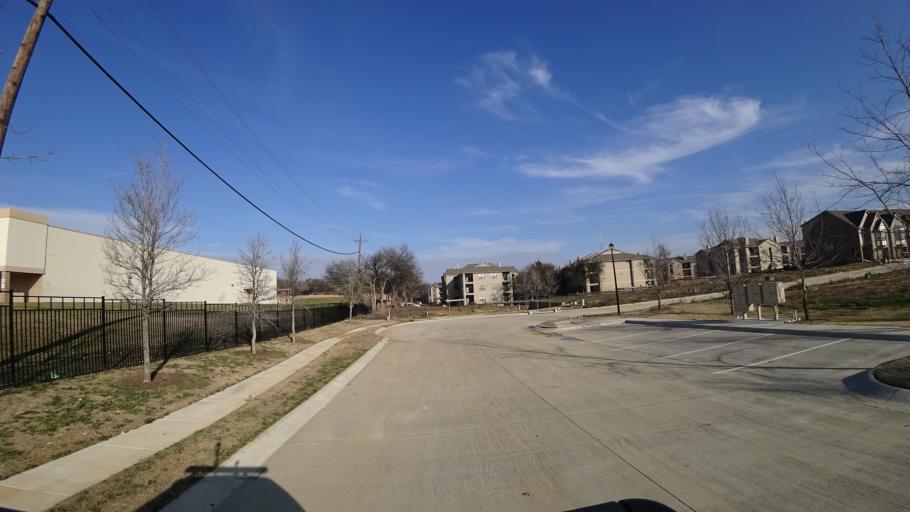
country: US
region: Texas
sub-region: Denton County
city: Lewisville
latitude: 33.0094
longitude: -96.9919
